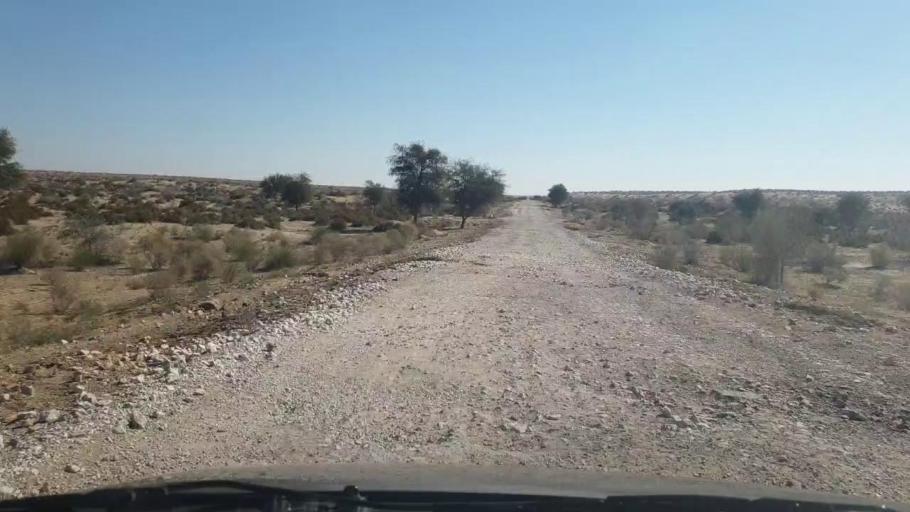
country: PK
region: Sindh
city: Bozdar
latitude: 27.0422
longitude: 68.6875
